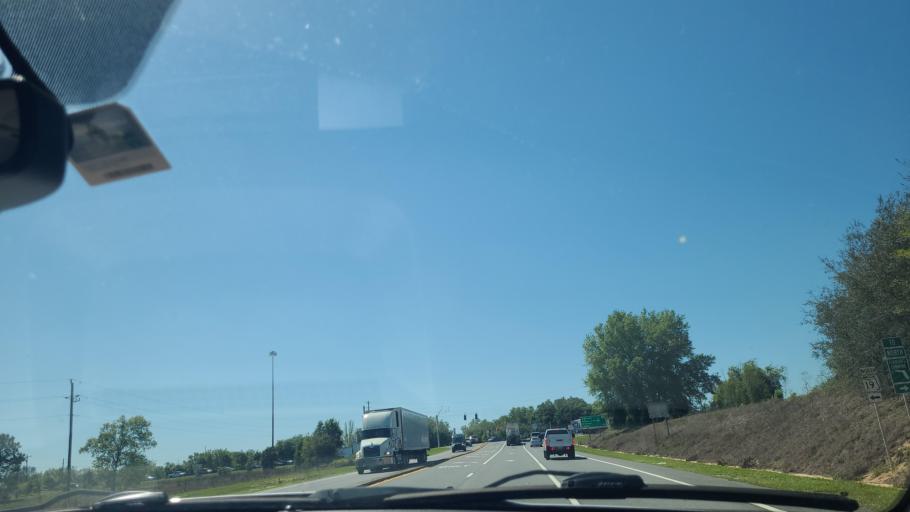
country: US
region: Florida
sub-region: Lake County
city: Howie In The Hills
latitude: 28.6448
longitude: -81.8093
